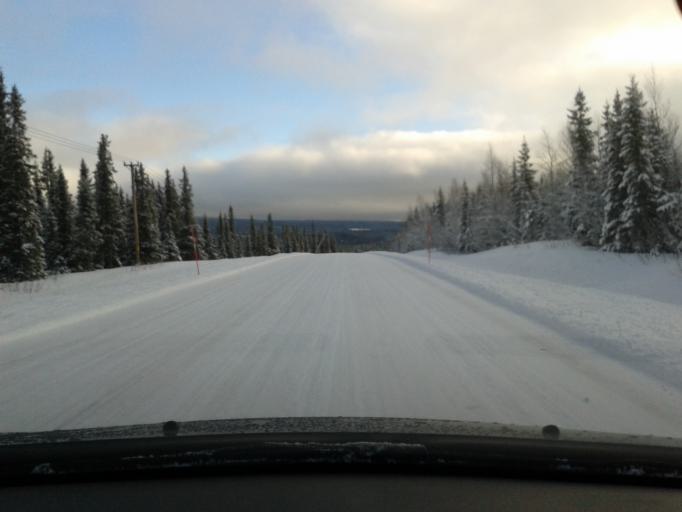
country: SE
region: Vaesterbotten
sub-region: Vilhelmina Kommun
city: Sjoberg
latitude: 65.2570
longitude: 15.6614
